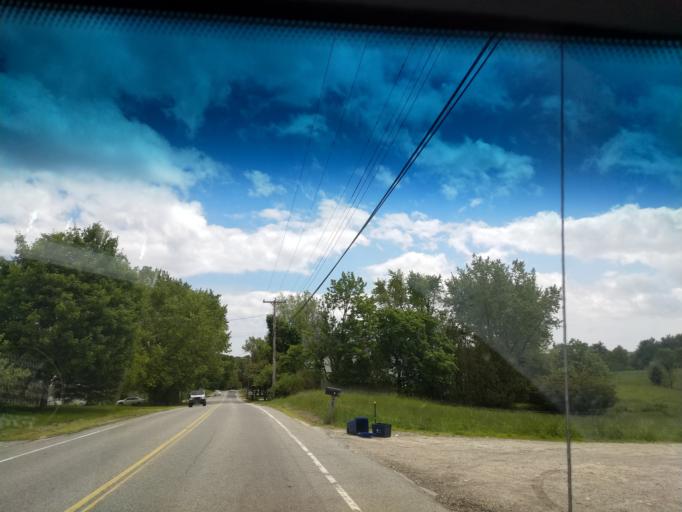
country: US
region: Maine
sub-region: Cumberland County
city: Falmouth
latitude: 43.7431
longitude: -70.2912
